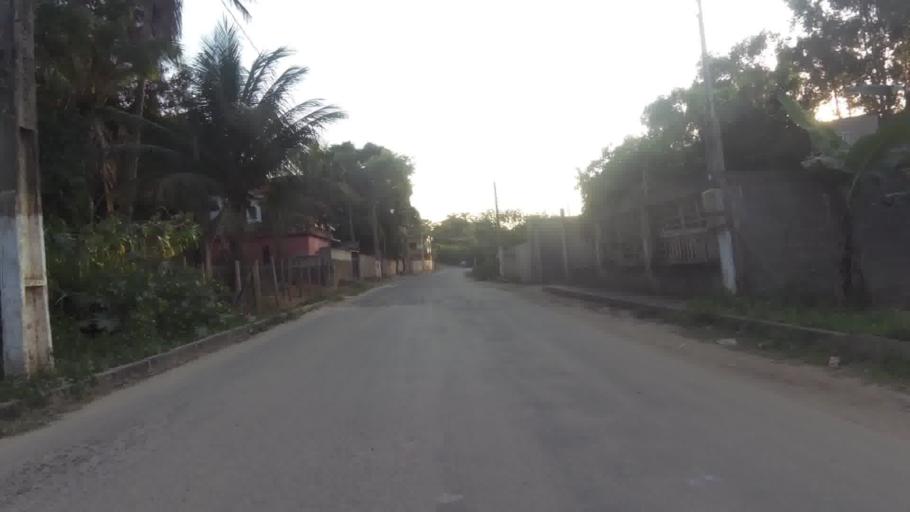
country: BR
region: Espirito Santo
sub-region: Piuma
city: Piuma
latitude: -20.8298
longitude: -40.7235
